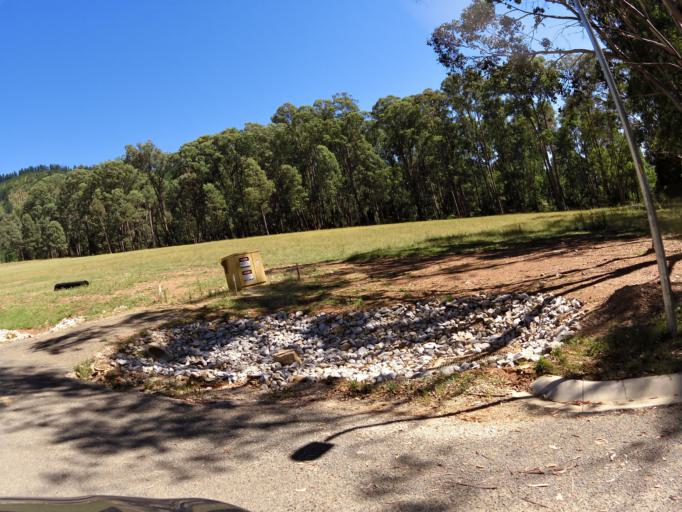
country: AU
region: Victoria
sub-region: Alpine
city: Mount Beauty
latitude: -36.7441
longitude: 146.9546
